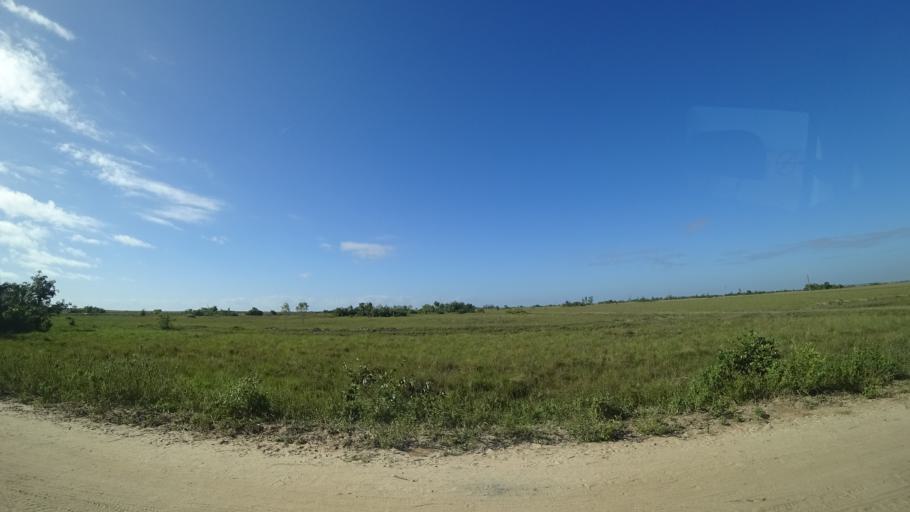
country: MZ
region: Sofala
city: Beira
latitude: -19.7320
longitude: 34.9785
